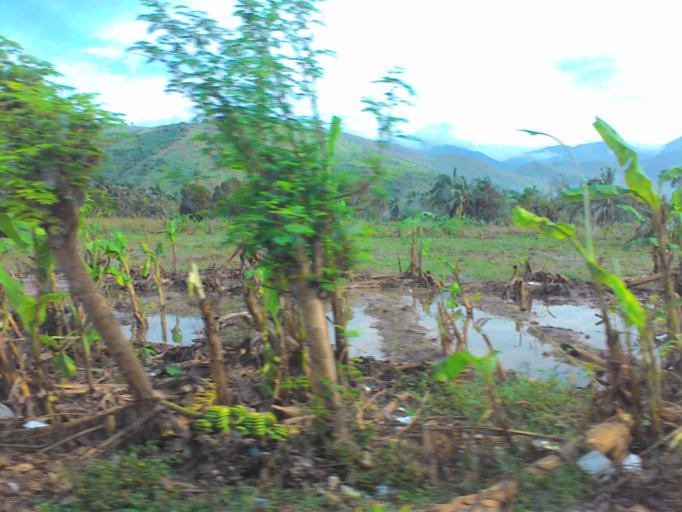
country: HT
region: Sud
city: Saint-Louis du Sud
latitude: 18.2679
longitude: -73.5940
